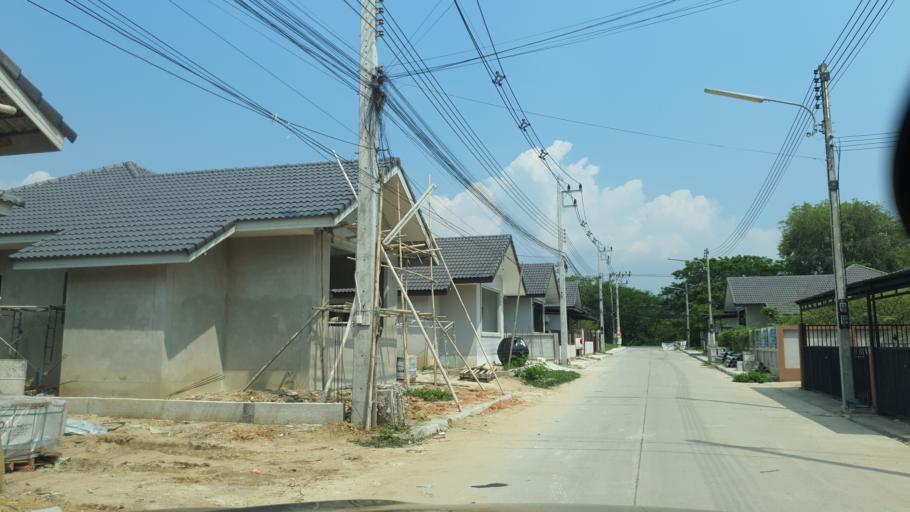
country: TH
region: Chiang Mai
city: San Kamphaeng
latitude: 18.7410
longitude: 99.1084
